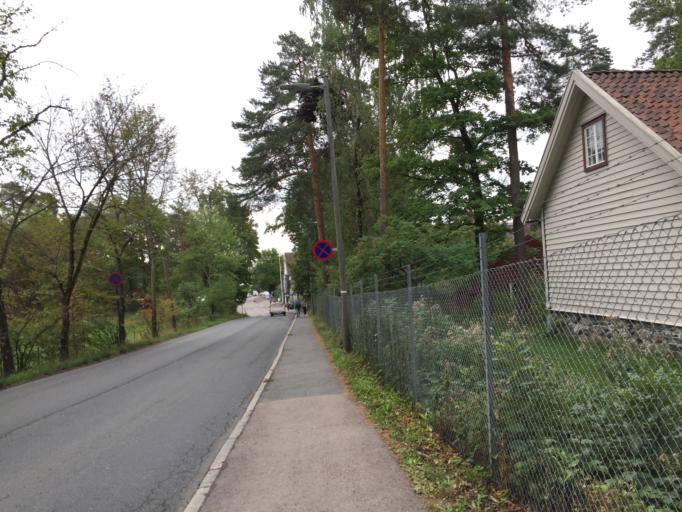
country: NO
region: Oslo
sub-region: Oslo
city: Sjolyststranda
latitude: 59.9085
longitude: 10.6849
